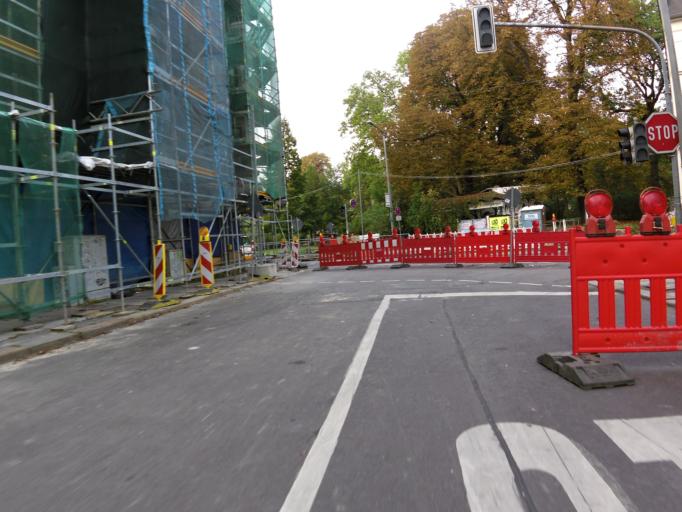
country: DE
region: Saxony
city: Leipzig
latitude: 51.3342
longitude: 12.4127
